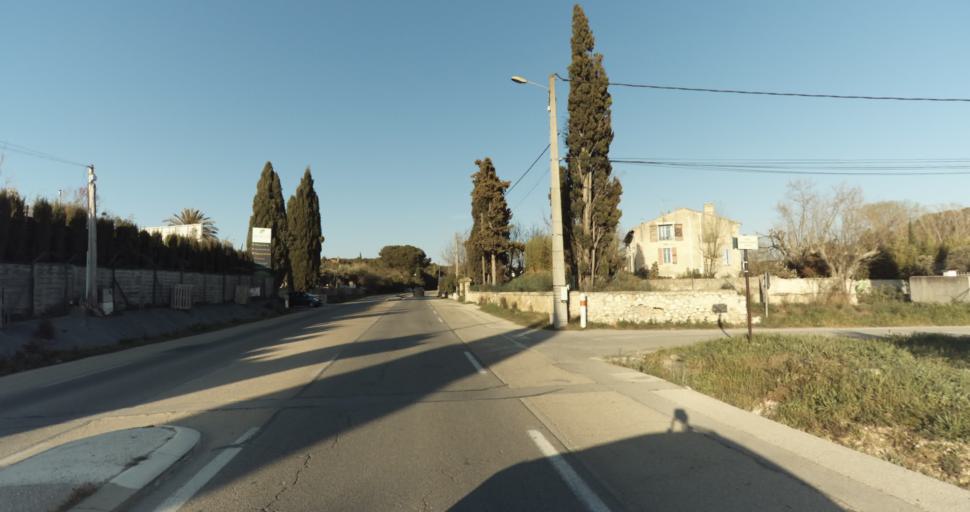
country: FR
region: Provence-Alpes-Cote d'Azur
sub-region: Departement des Bouches-du-Rhone
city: Ventabren
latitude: 43.5434
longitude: 5.2760
